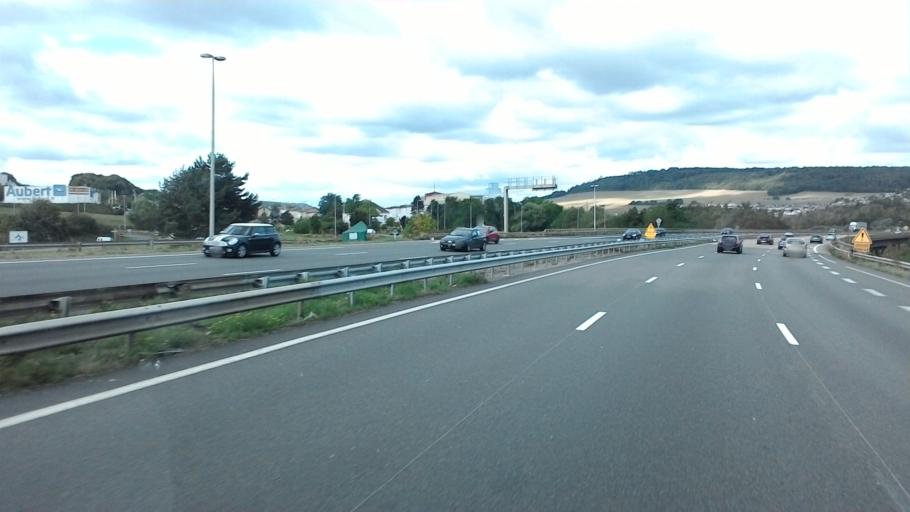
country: FR
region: Lorraine
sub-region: Departement de Meurthe-et-Moselle
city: Champigneulles
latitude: 48.7433
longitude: 6.1529
